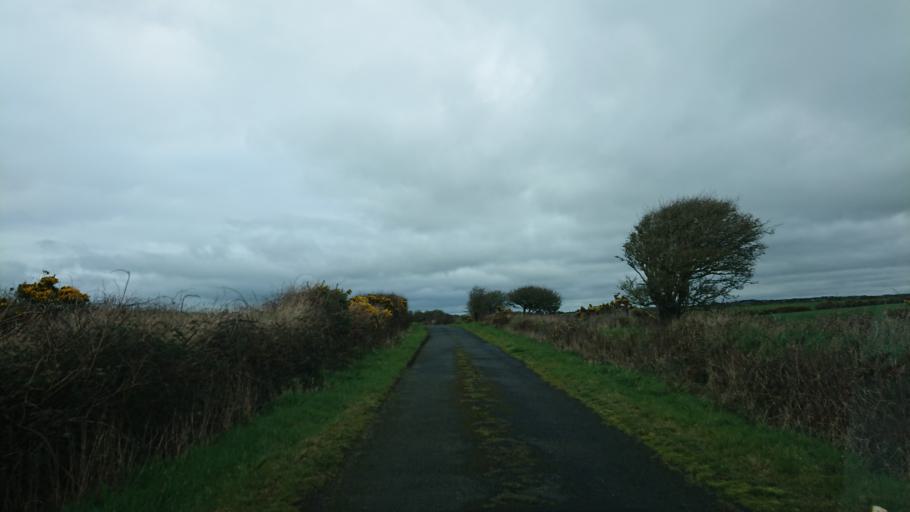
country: IE
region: Munster
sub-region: Waterford
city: Dunmore East
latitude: 52.1472
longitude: -7.0407
